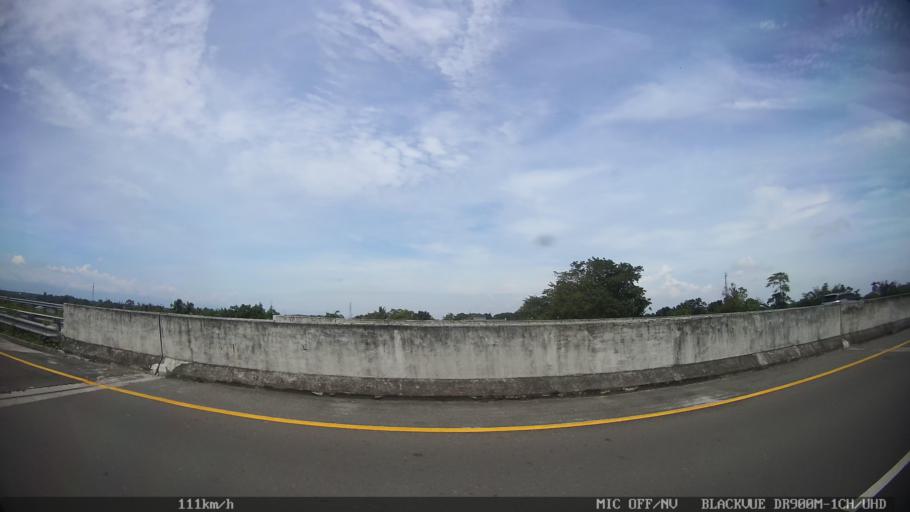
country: ID
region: North Sumatra
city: Percut
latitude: 3.5509
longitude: 98.8523
